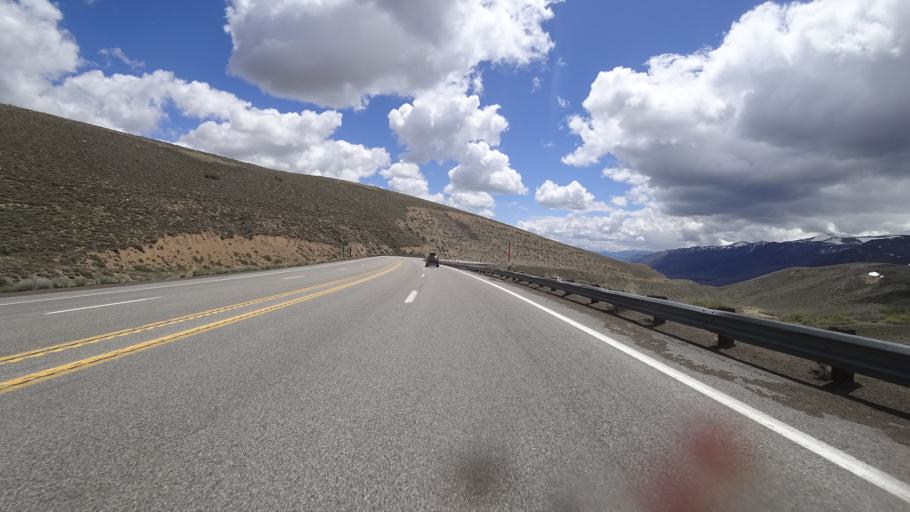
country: US
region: California
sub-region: Mono County
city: Bridgeport
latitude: 38.0860
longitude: -119.1813
